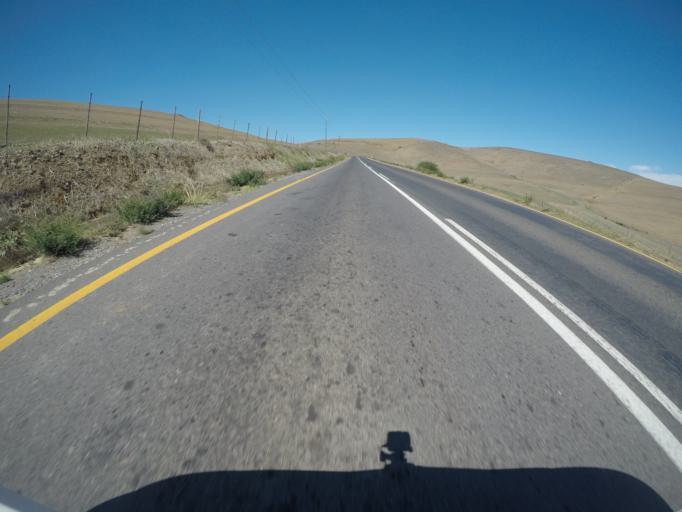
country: ZA
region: Western Cape
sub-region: City of Cape Town
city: Kraaifontein
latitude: -33.7970
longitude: 18.6076
